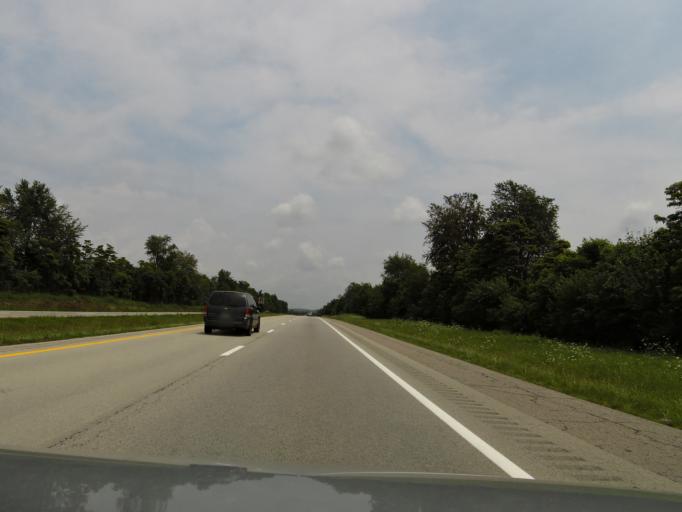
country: US
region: Kentucky
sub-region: Hardin County
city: Elizabethtown
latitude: 37.6408
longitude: -85.9216
